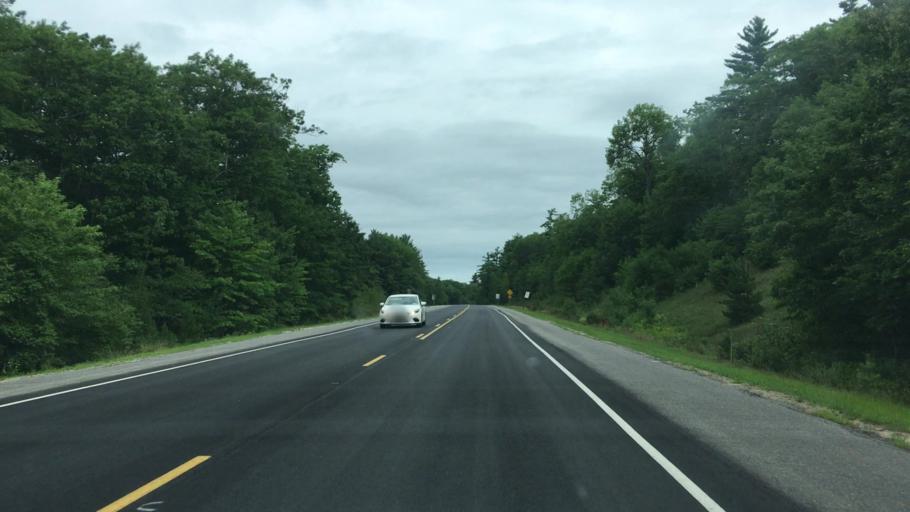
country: US
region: Maine
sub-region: Washington County
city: Cherryfield
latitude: 44.9027
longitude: -67.8562
